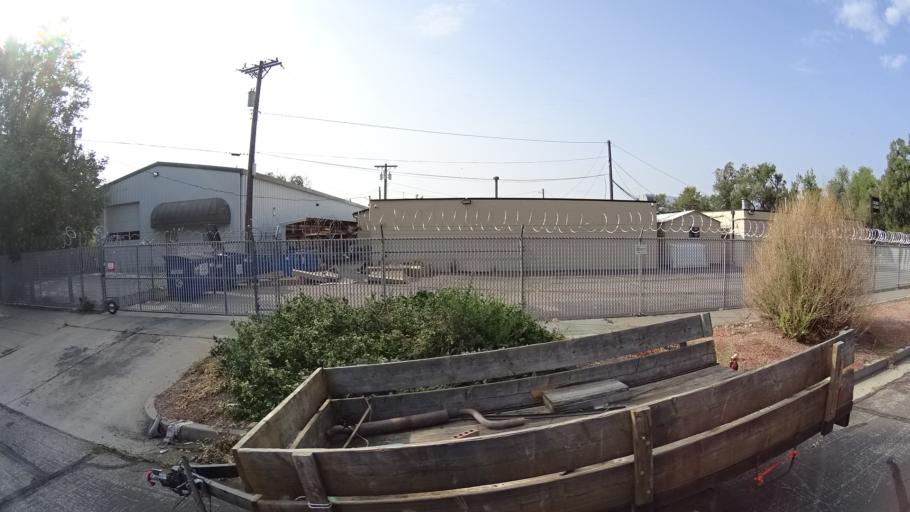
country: US
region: Colorado
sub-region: El Paso County
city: Colorado Springs
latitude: 38.8397
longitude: -104.7896
